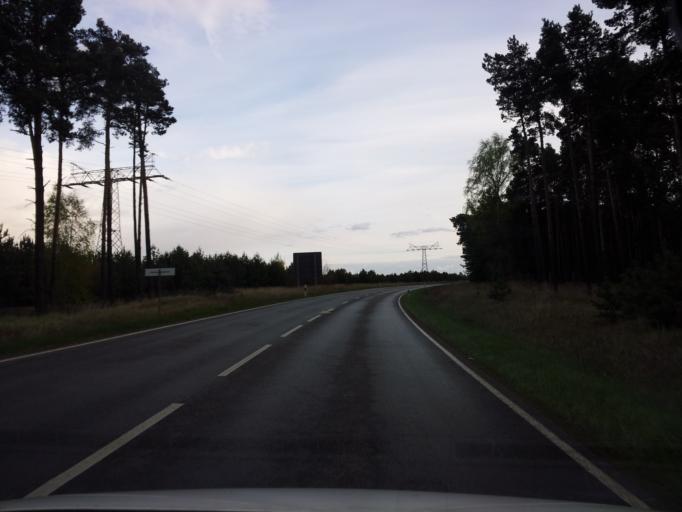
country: DE
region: Brandenburg
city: Heinersbruck
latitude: 51.8285
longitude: 14.5215
